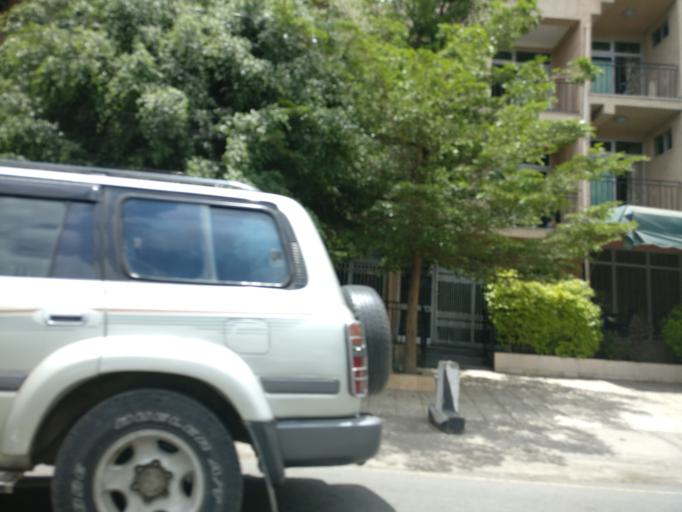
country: ET
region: Oromiya
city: Bishoftu
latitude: 8.7509
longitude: 38.9673
